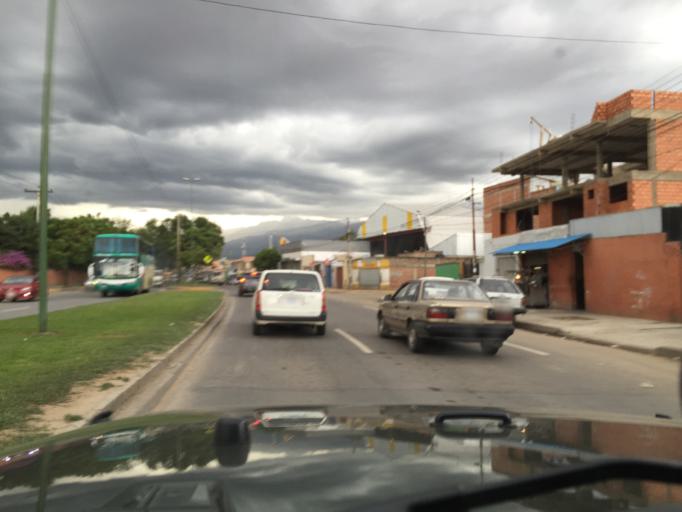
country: BO
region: Cochabamba
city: Cochabamba
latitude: -17.4074
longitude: -66.1758
